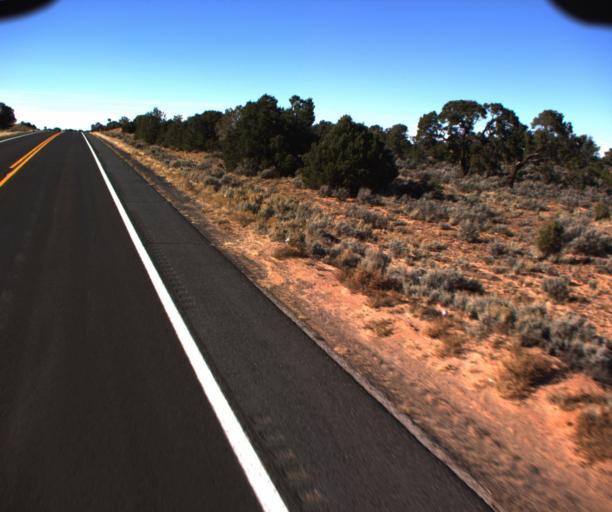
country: US
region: Arizona
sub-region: Coconino County
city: Kaibito
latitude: 36.5860
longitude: -110.8691
